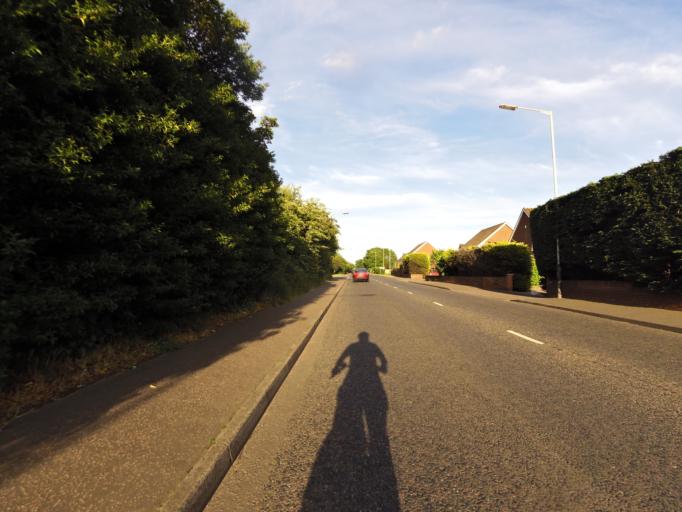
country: GB
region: England
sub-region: Norfolk
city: Norwich
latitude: 52.6665
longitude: 1.2748
